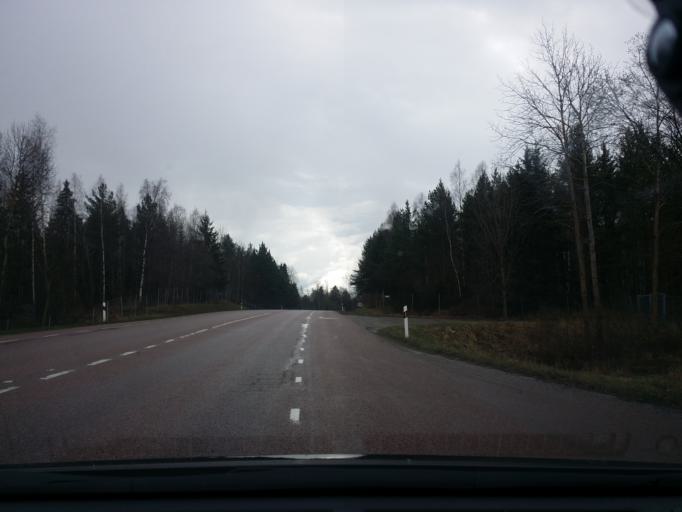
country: SE
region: Uppsala
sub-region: Enkopings Kommun
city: Enkoping
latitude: 59.6647
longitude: 17.0718
